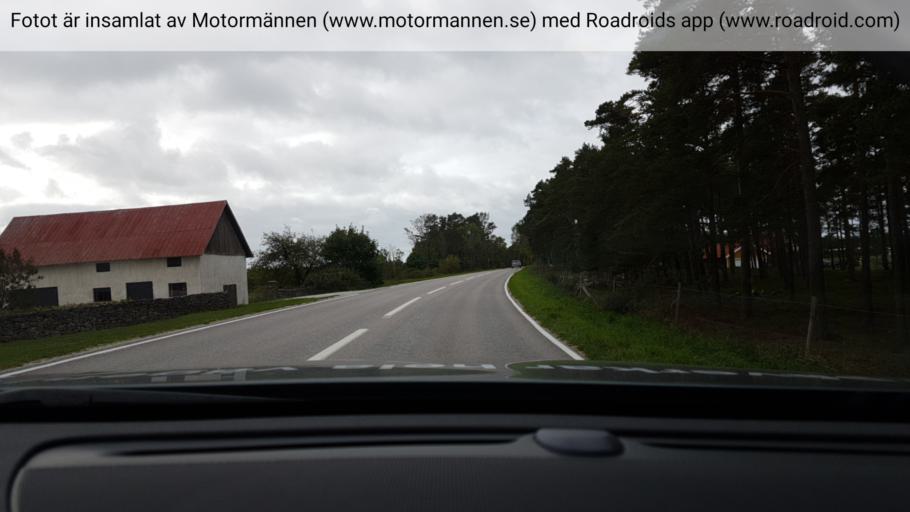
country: SE
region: Gotland
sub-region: Gotland
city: Klintehamn
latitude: 57.3248
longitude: 18.1918
